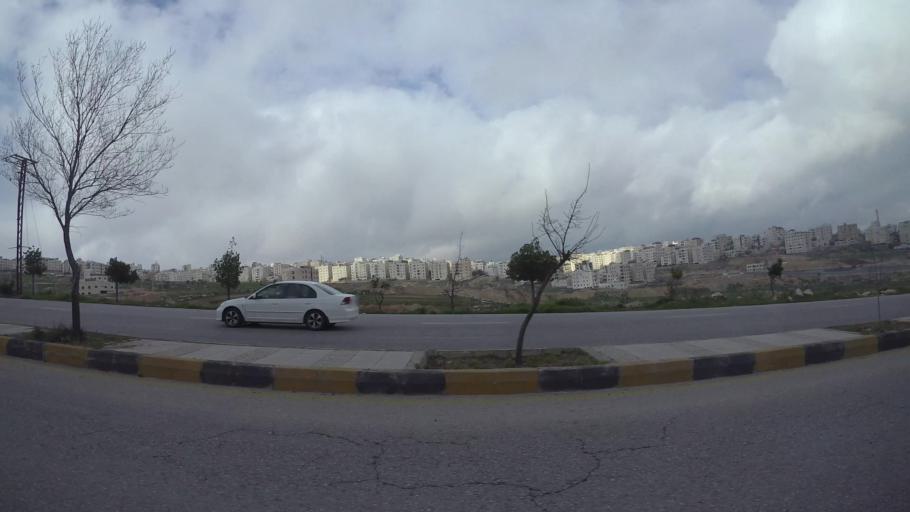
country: JO
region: Amman
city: Al Jubayhah
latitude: 32.0409
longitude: 35.8805
